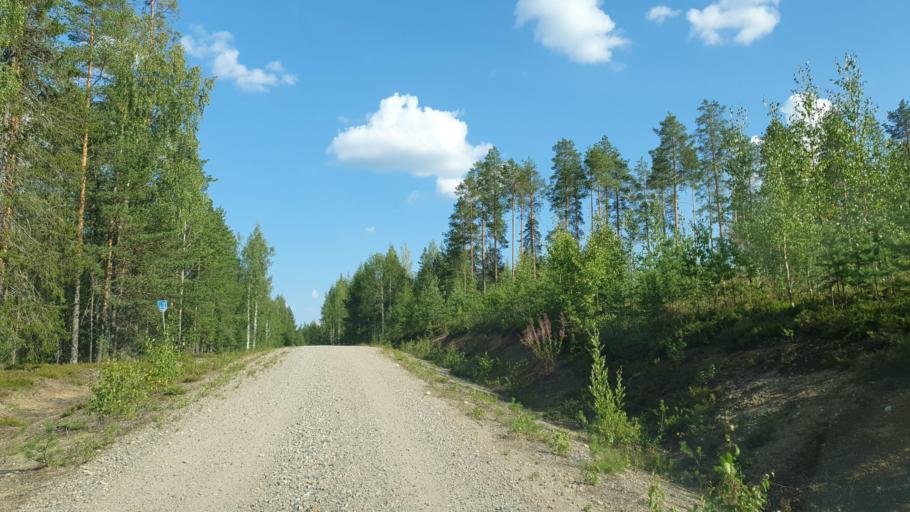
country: FI
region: Kainuu
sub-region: Kehys-Kainuu
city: Kuhmo
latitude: 63.9534
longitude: 29.5589
